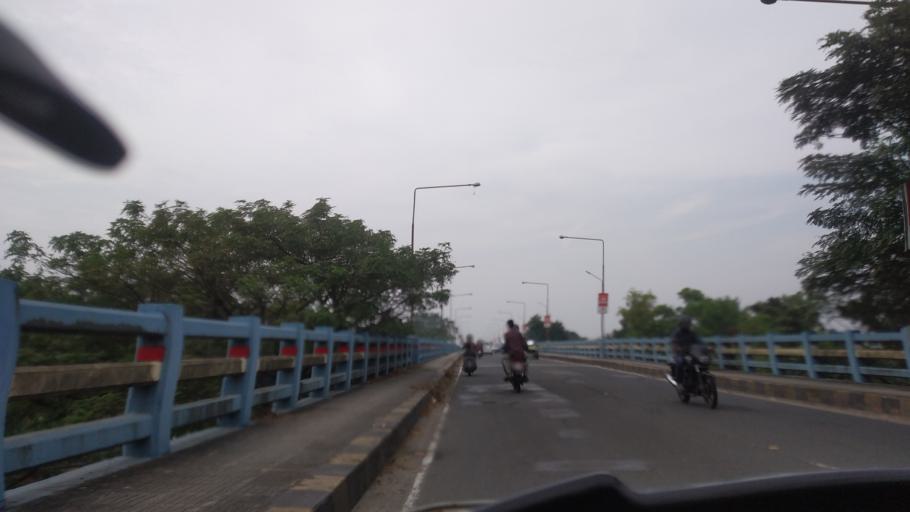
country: IN
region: Kerala
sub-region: Ernakulam
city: Elur
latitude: 10.0710
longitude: 76.2835
